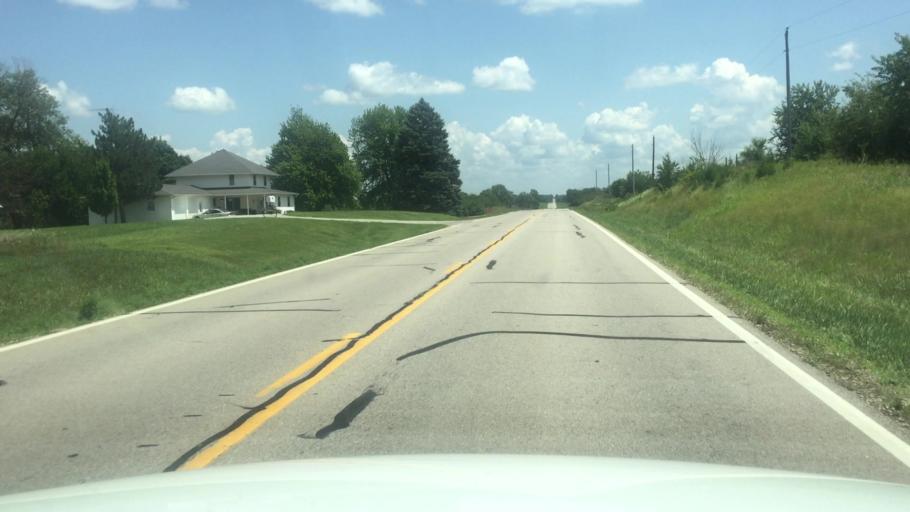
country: US
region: Kansas
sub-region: Brown County
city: Horton
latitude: 39.6674
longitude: -95.5782
